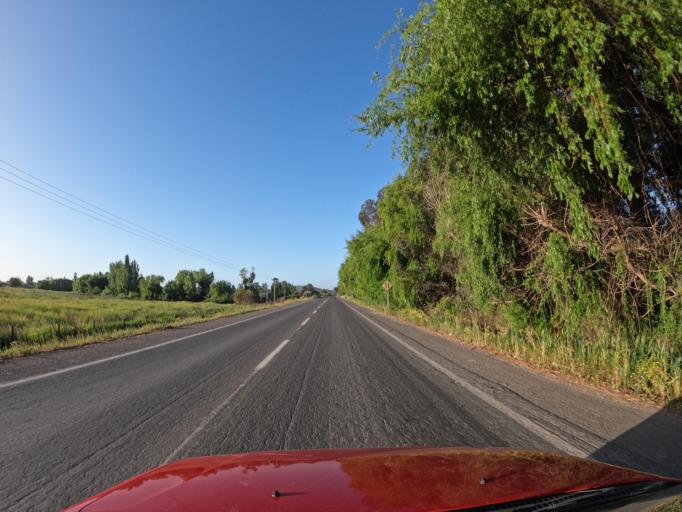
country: CL
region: O'Higgins
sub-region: Provincia de Colchagua
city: Santa Cruz
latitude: -34.3614
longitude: -71.4133
